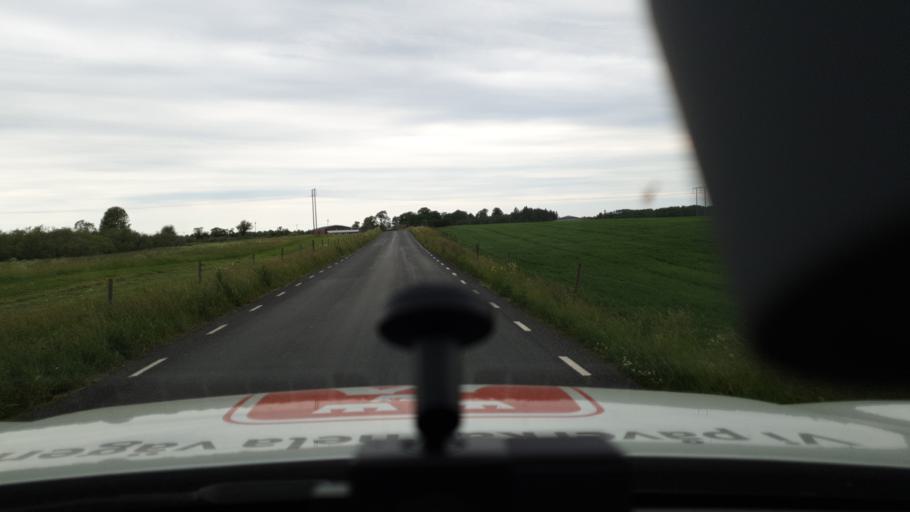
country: SE
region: Vaestra Goetaland
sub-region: Falkopings Kommun
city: Falkoeping
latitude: 58.0973
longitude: 13.4942
